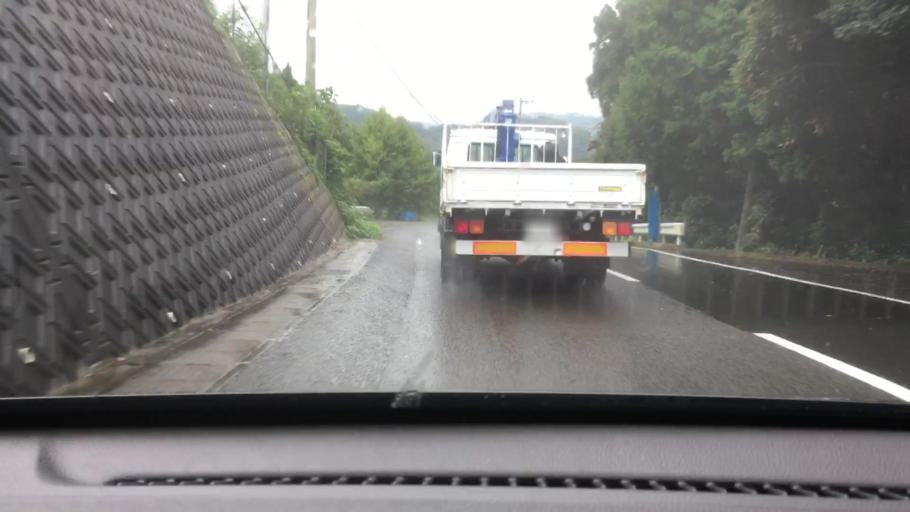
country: JP
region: Nagasaki
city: Togitsu
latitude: 32.8671
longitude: 129.7694
